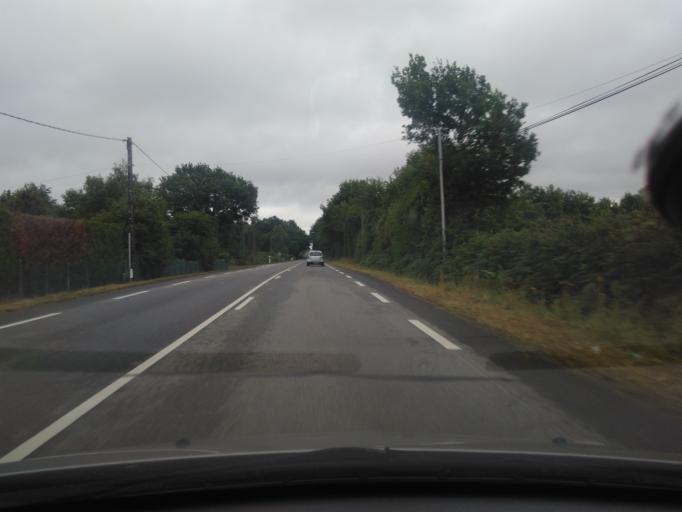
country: FR
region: Pays de la Loire
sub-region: Departement de la Vendee
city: Nesmy
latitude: 46.6182
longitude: -1.3601
